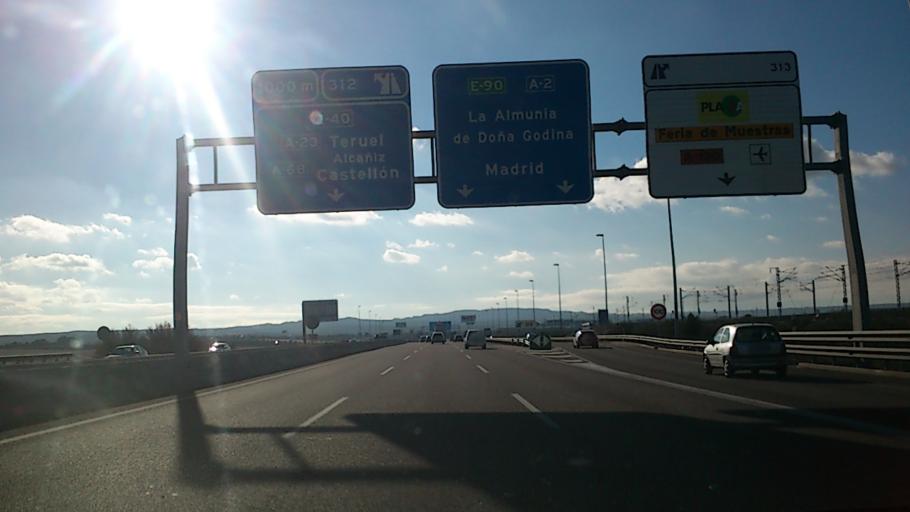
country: ES
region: Aragon
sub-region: Provincia de Zaragoza
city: Montecanal
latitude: 41.6470
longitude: -0.9657
